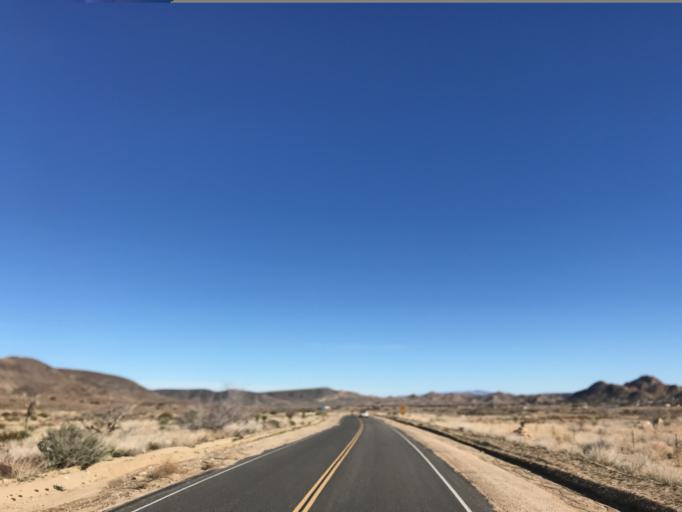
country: US
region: California
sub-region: San Bernardino County
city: Yucca Valley
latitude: 34.1630
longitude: -116.5181
